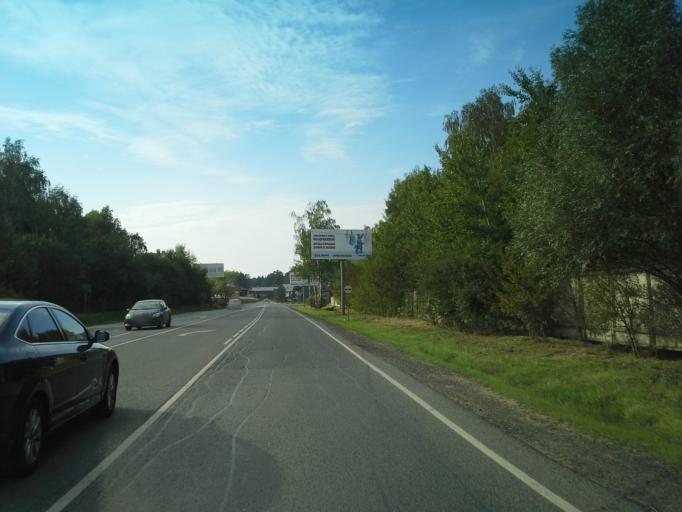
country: RU
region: Moskovskaya
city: Gorki Vtoryye
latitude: 55.6829
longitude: 37.1425
